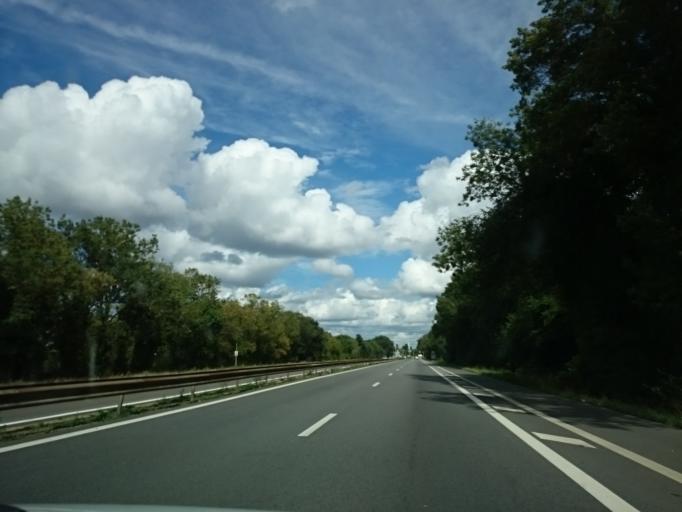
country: FR
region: Pays de la Loire
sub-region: Departement de la Loire-Atlantique
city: Reze
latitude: 47.1892
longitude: -1.5824
